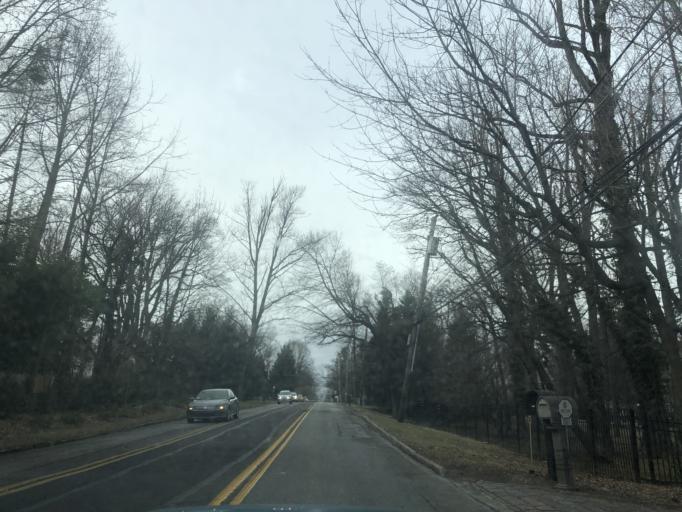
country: US
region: Pennsylvania
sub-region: Delaware County
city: Radnor
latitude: 40.0394
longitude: -75.3309
